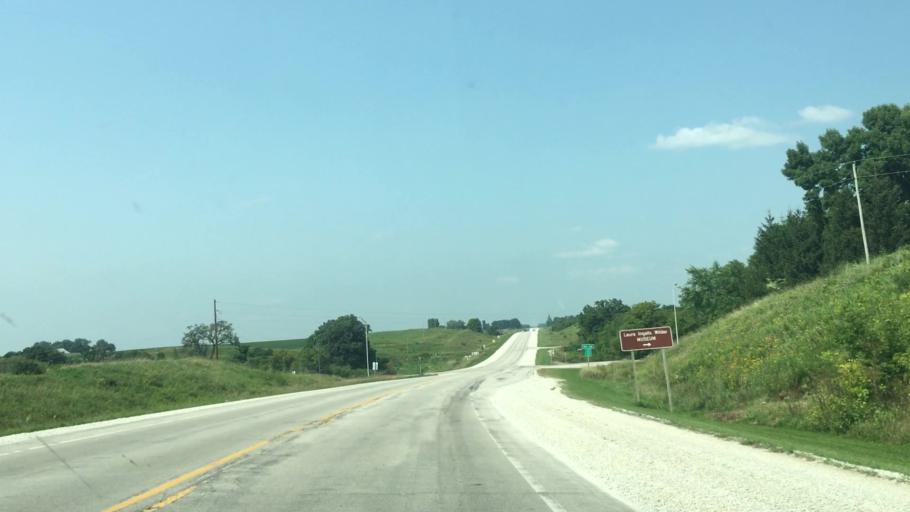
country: US
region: Minnesota
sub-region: Fillmore County
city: Harmony
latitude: 43.4561
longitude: -91.8695
